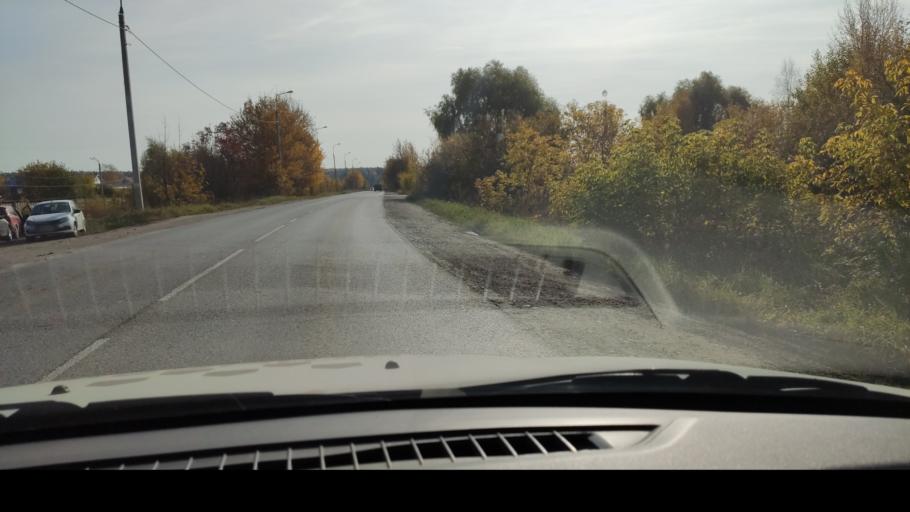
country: RU
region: Perm
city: Novyye Lyady
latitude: 58.0458
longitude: 56.5920
